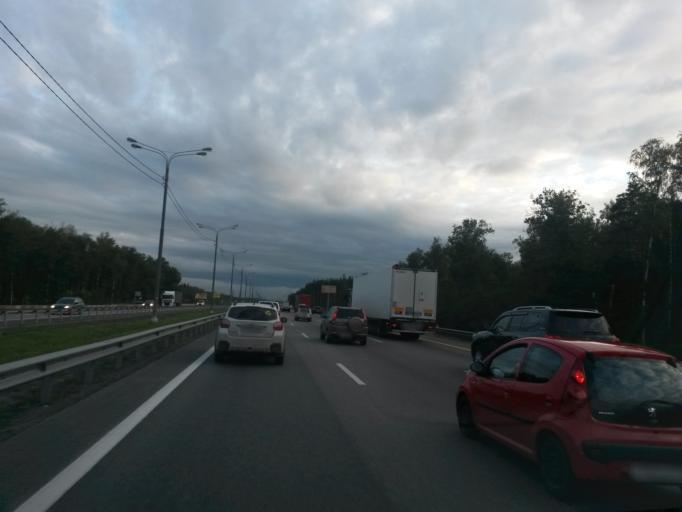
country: RU
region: Moskovskaya
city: Vostryakovo
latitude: 55.4299
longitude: 37.7979
